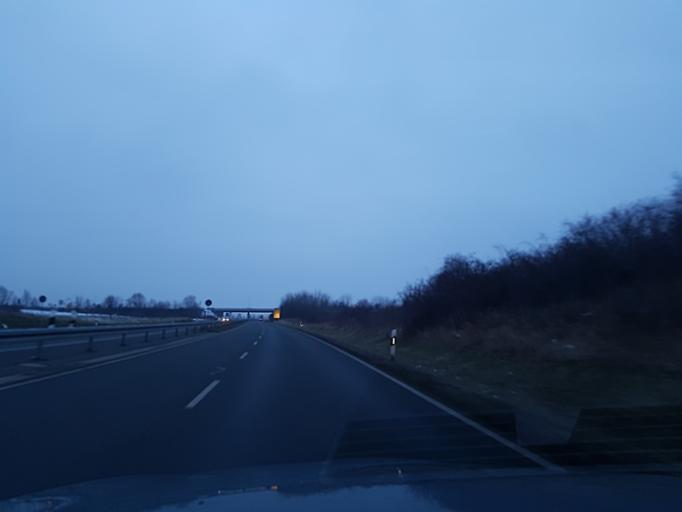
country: DE
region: Saxony
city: Riesa
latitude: 51.2987
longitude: 13.2813
